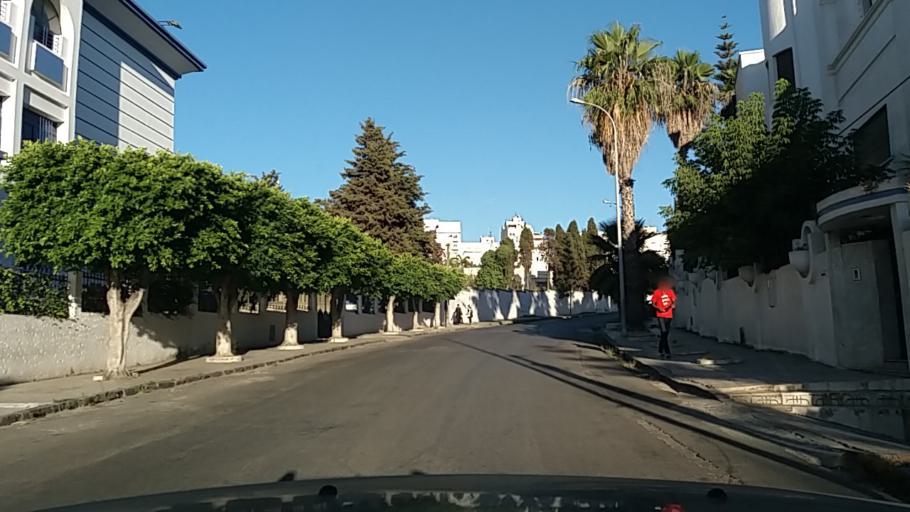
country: MA
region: Tanger-Tetouan
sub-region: Tanger-Assilah
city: Tangier
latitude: 35.7823
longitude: -5.8269
